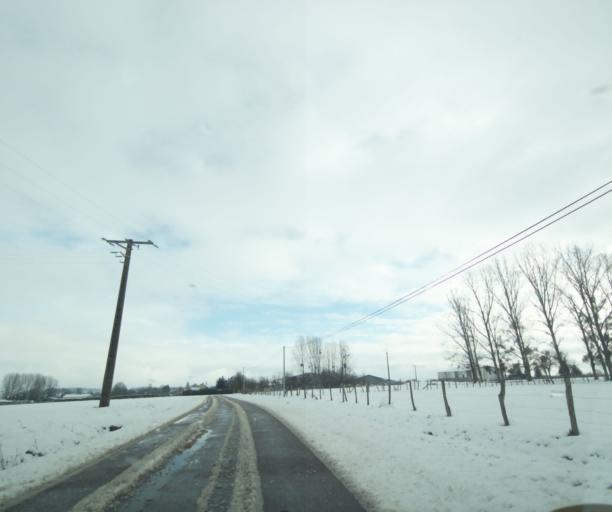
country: FR
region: Champagne-Ardenne
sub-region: Departement de la Haute-Marne
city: Montier-en-Der
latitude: 48.4538
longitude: 4.6680
